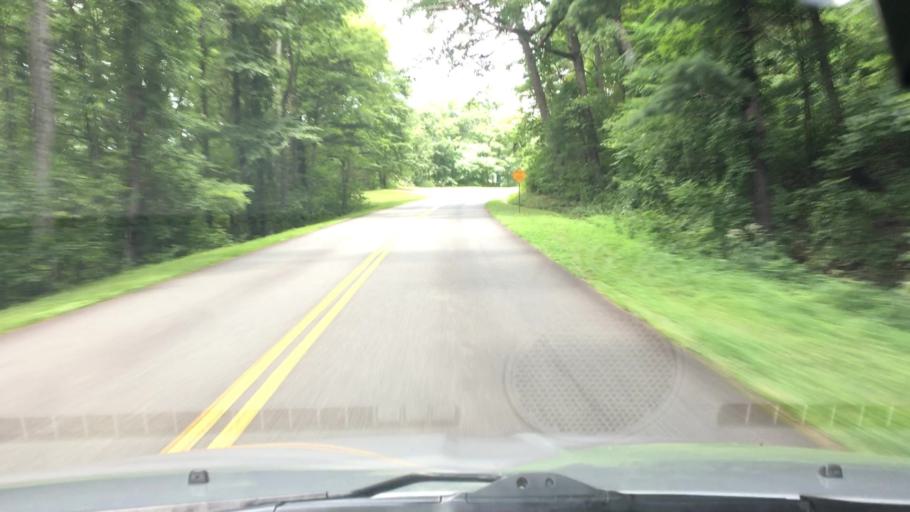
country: US
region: North Carolina
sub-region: Buncombe County
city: Asheville
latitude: 35.6078
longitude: -82.4938
